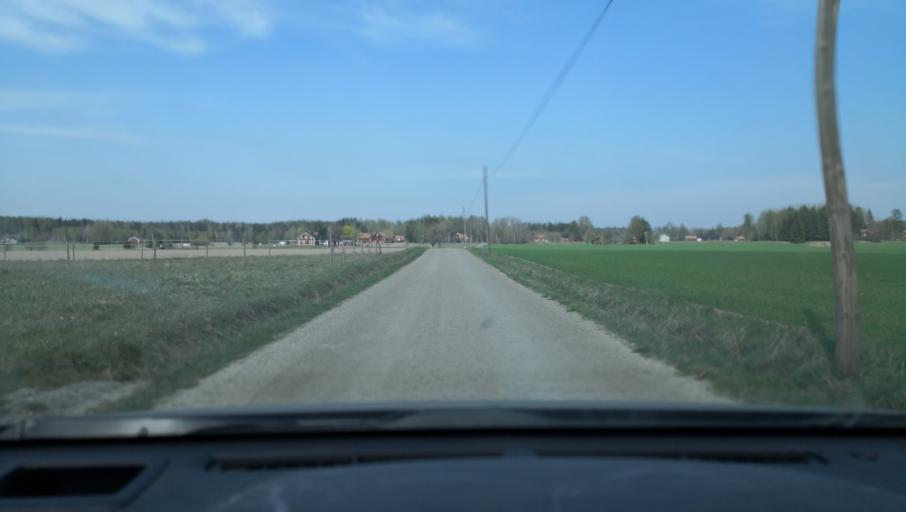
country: SE
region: Vaestmanland
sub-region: Vasteras
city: Skultuna
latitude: 59.7982
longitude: 16.4363
